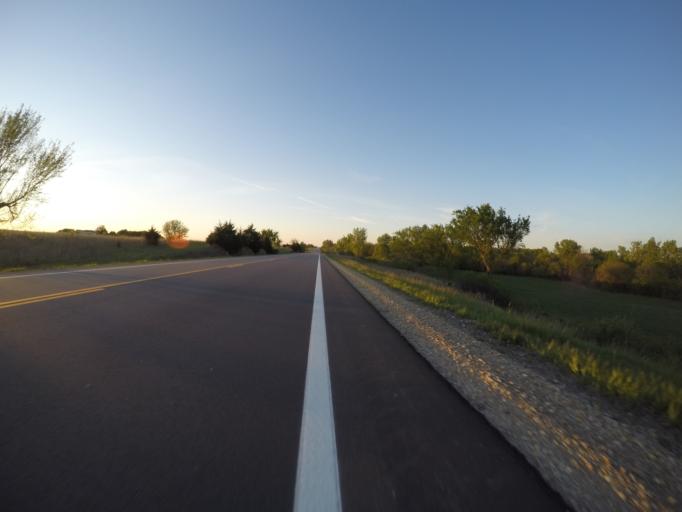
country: US
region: Kansas
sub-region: Pottawatomie County
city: Westmoreland
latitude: 39.4182
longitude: -96.5199
